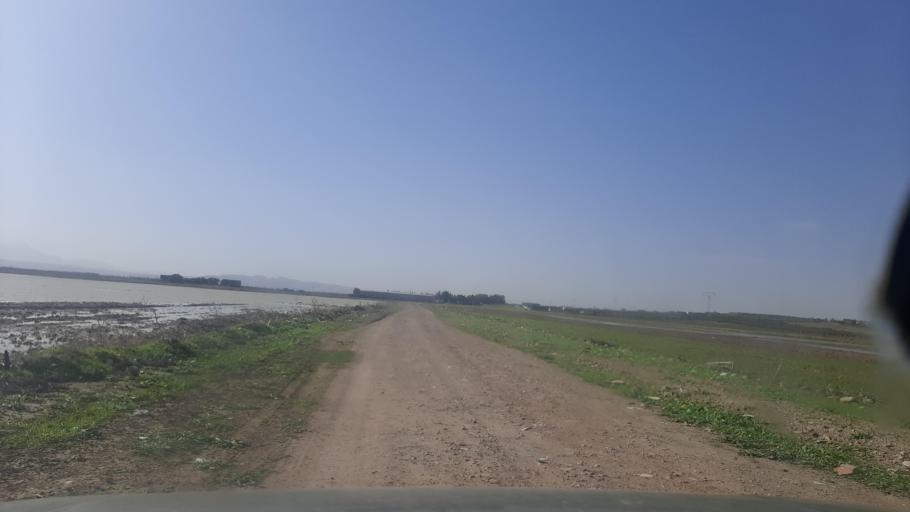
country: TN
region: Tunis
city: La Mohammedia
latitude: 36.6507
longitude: 10.0879
